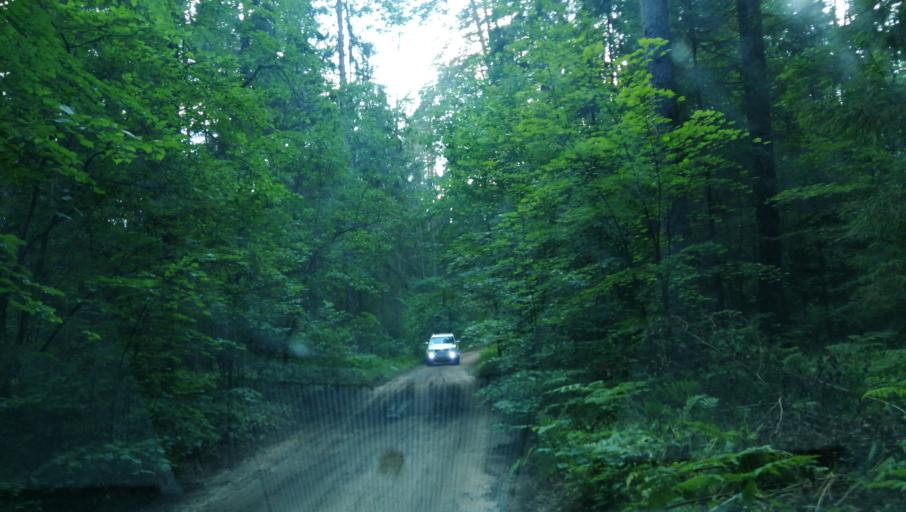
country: LV
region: Cesu Rajons
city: Cesis
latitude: 57.2900
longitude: 25.1991
